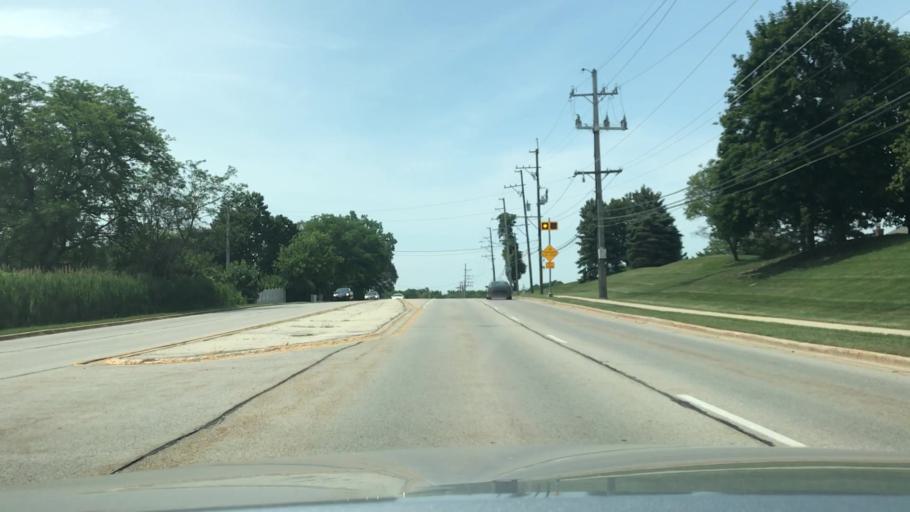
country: US
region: Illinois
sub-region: DuPage County
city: Woodridge
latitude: 41.7323
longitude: -88.0122
